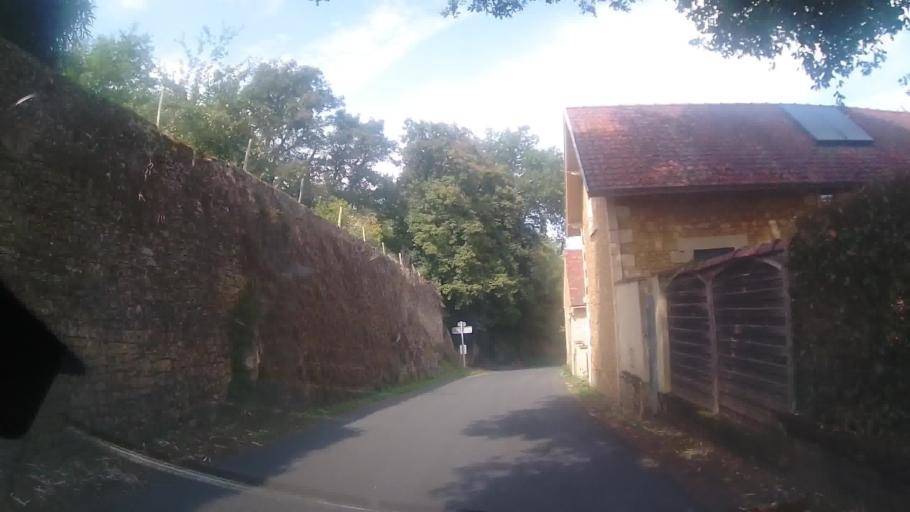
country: FR
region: Aquitaine
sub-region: Departement de la Dordogne
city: Carsac-Aillac
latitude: 44.8326
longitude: 1.3105
